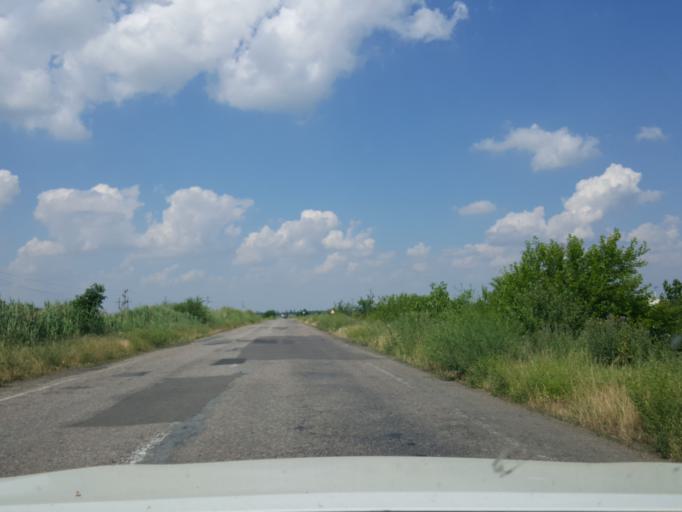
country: UA
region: Odessa
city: Starokozache
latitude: 46.4019
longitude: 30.1007
